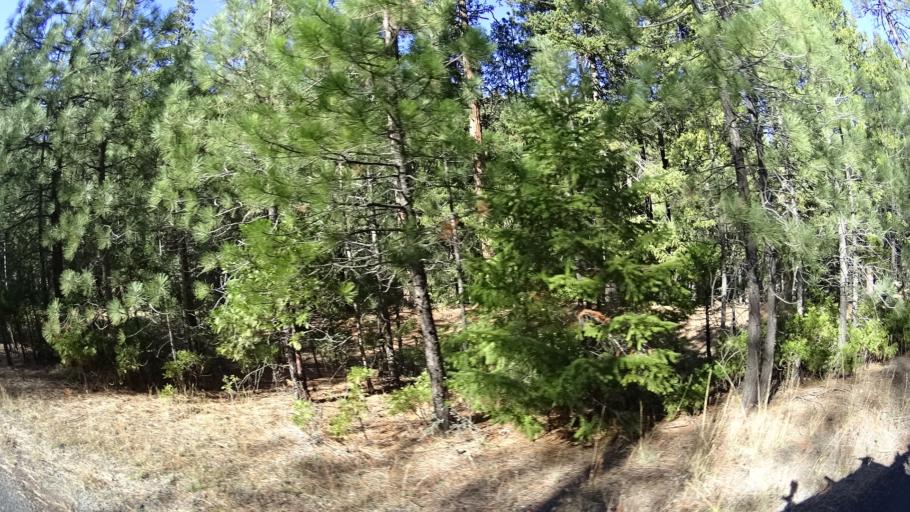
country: US
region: California
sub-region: Siskiyou County
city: Weed
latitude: 41.4214
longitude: -122.5023
